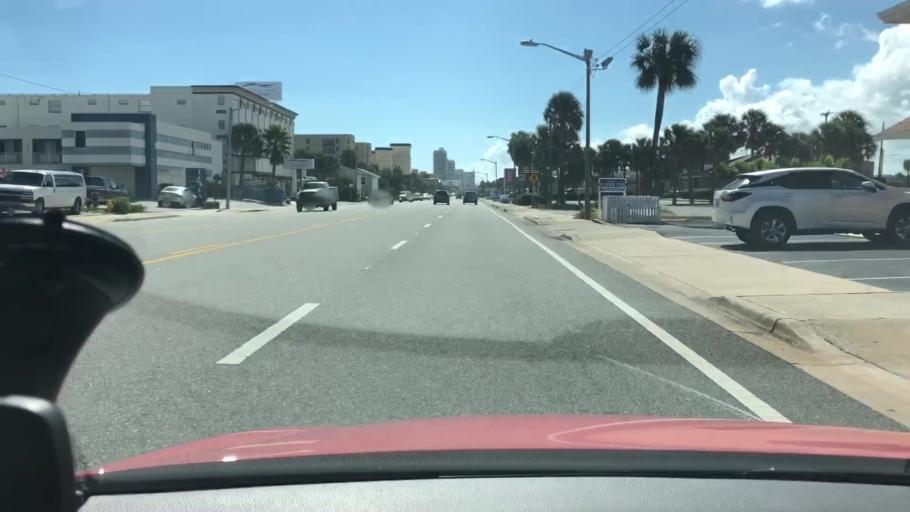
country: US
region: Florida
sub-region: Volusia County
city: Ormond Beach
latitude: 29.2795
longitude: -81.0339
